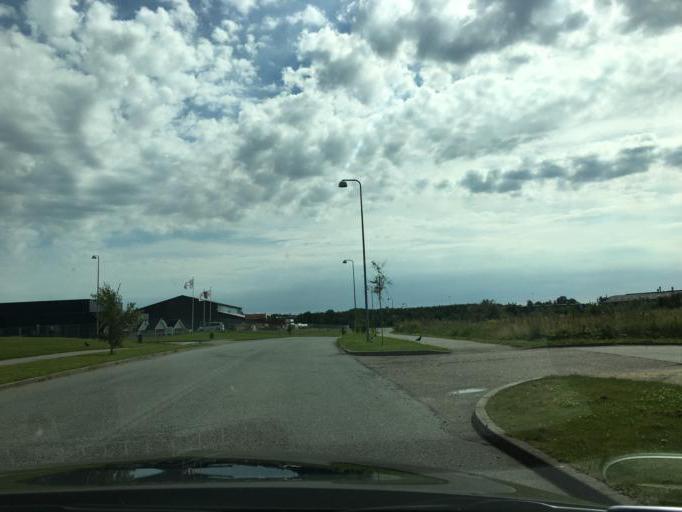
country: DK
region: South Denmark
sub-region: Kolding Kommune
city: Kolding
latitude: 55.5415
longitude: 9.4666
